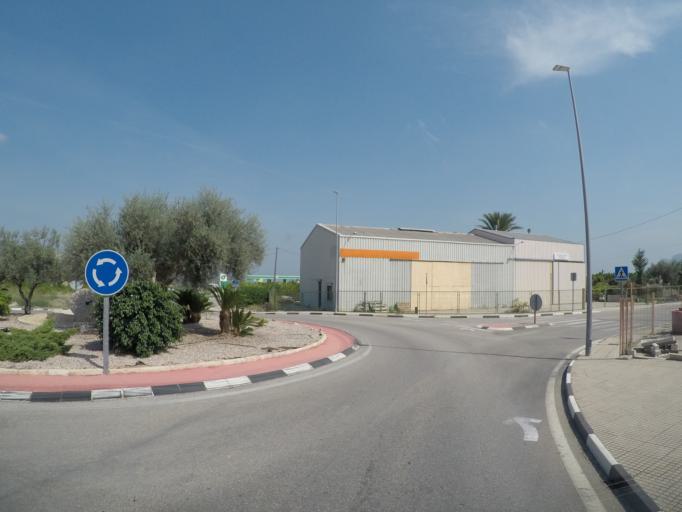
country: ES
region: Valencia
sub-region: Provincia de Alicante
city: Pego
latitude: 38.8487
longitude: -0.1138
